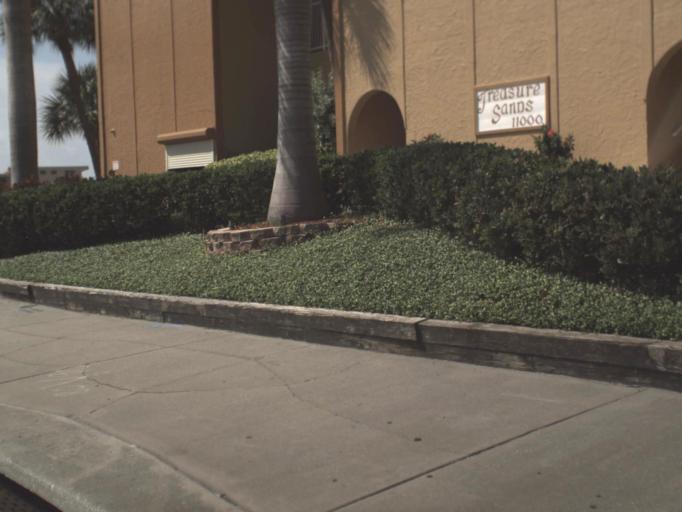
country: US
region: Florida
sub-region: Pinellas County
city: Treasure Island
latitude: 27.7708
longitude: -82.7711
